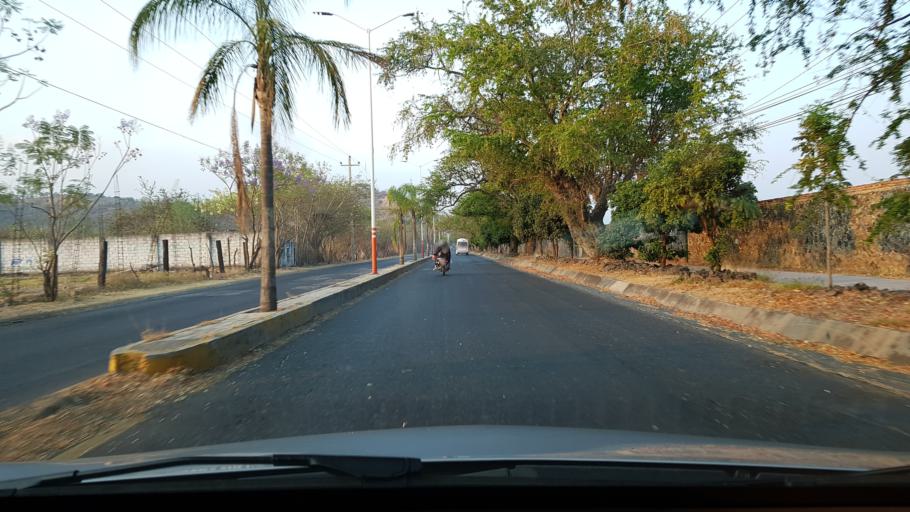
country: MX
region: Morelos
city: Jonacatepec de Leandro Valle
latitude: 18.6730
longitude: -98.8050
